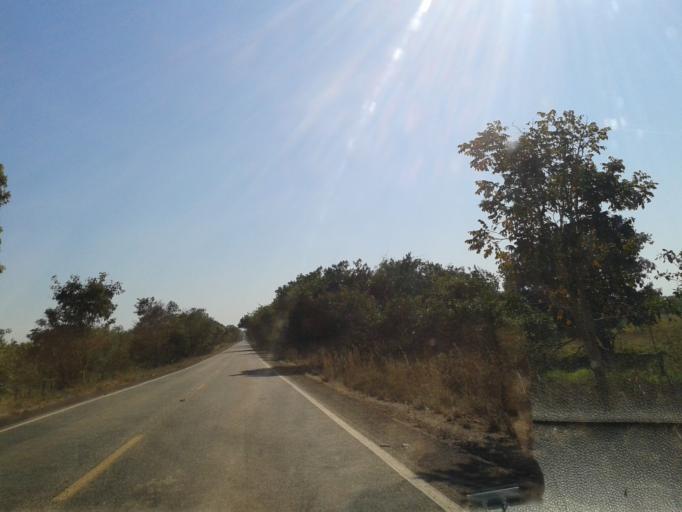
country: BR
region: Goias
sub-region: Mozarlandia
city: Mozarlandia
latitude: -14.5863
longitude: -50.5064
